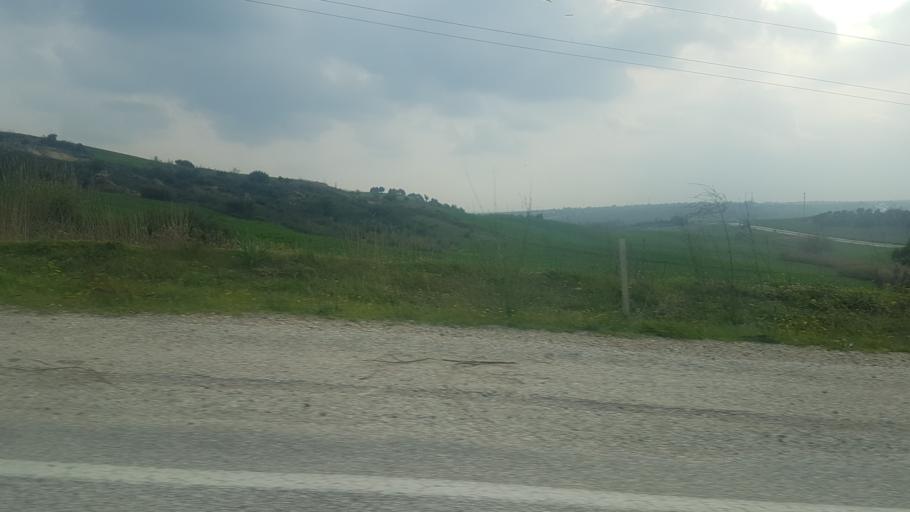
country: TR
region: Adana
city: Seyhan
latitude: 37.0447
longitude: 35.1818
